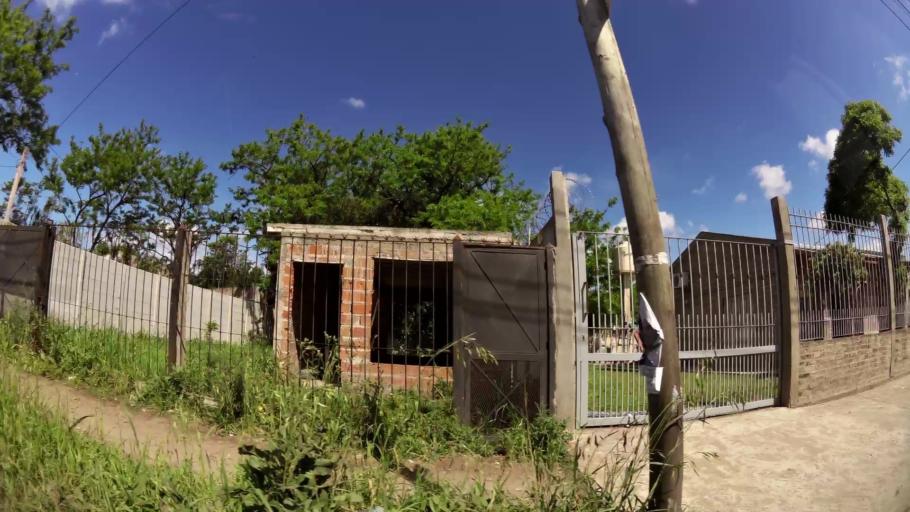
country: AR
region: Buenos Aires
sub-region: Partido de Quilmes
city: Quilmes
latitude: -34.8134
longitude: -58.2609
